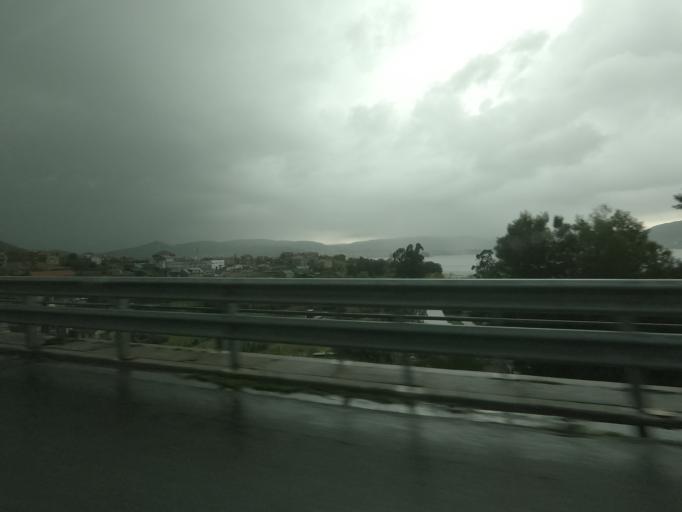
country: ES
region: Galicia
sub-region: Provincia de Pontevedra
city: Redondela
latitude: 42.3226
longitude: -8.6571
